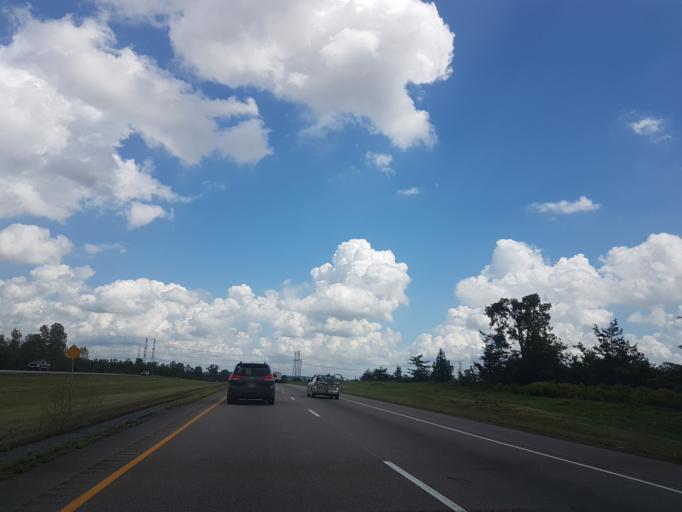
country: CA
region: Ontario
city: Deseronto
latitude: 44.2499
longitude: -77.0231
